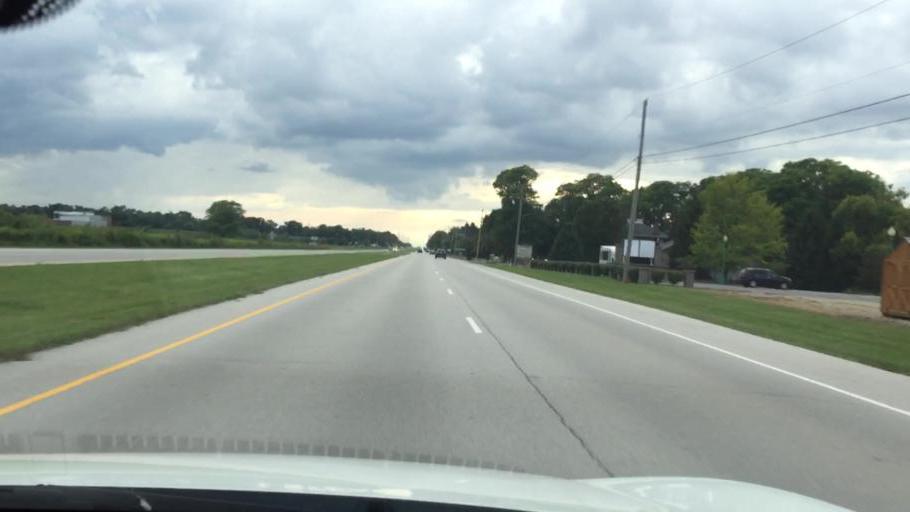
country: US
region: Ohio
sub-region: Clark County
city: Springfield
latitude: 39.9233
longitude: -83.7174
